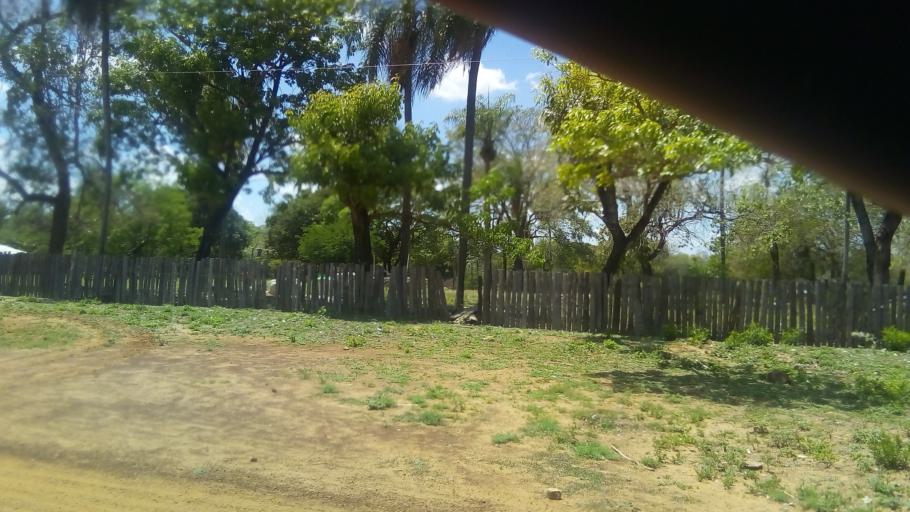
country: PY
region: Cordillera
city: Arroyos y Esteros
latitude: -24.9957
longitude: -57.2157
